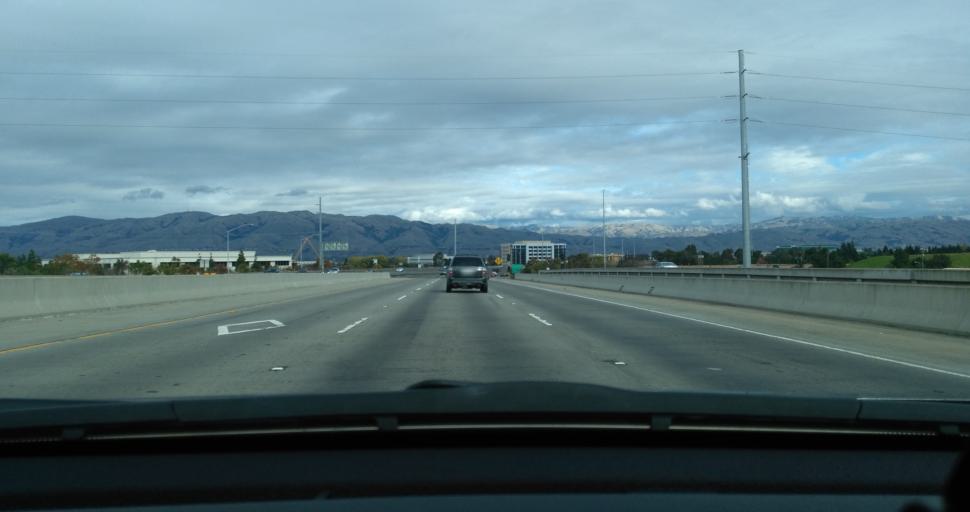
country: US
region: California
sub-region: Santa Clara County
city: Santa Clara
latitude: 37.4170
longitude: -121.9742
